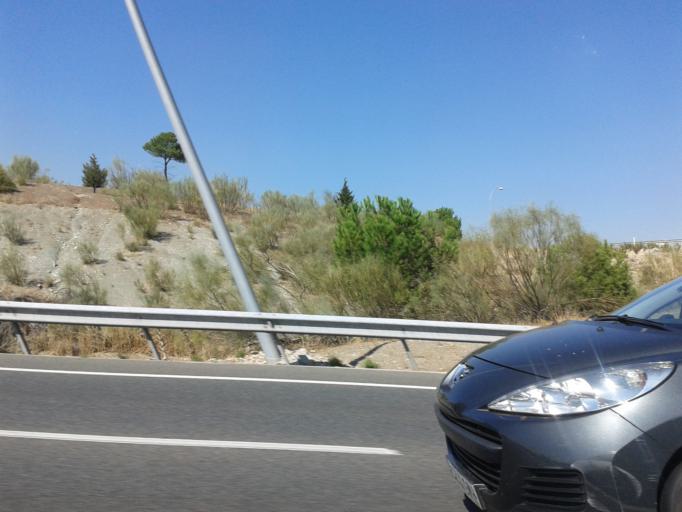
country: ES
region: Madrid
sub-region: Provincia de Madrid
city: Torrejon de Ardoz
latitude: 40.4566
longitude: -3.5055
